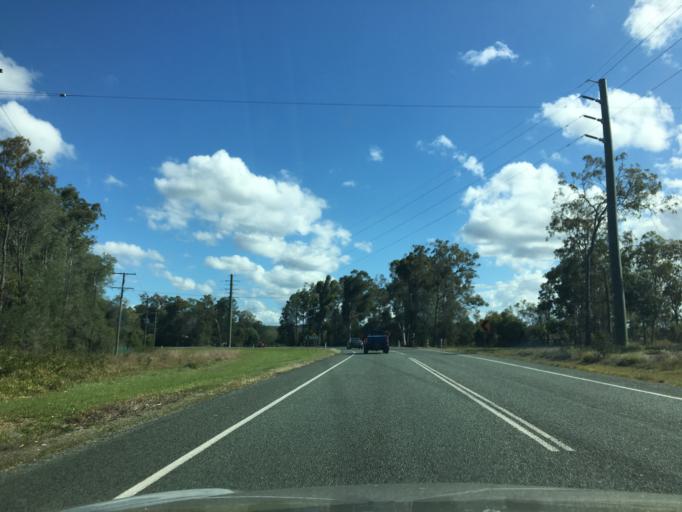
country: AU
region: Queensland
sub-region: Logan
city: Chambers Flat
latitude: -27.7818
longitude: 153.0994
